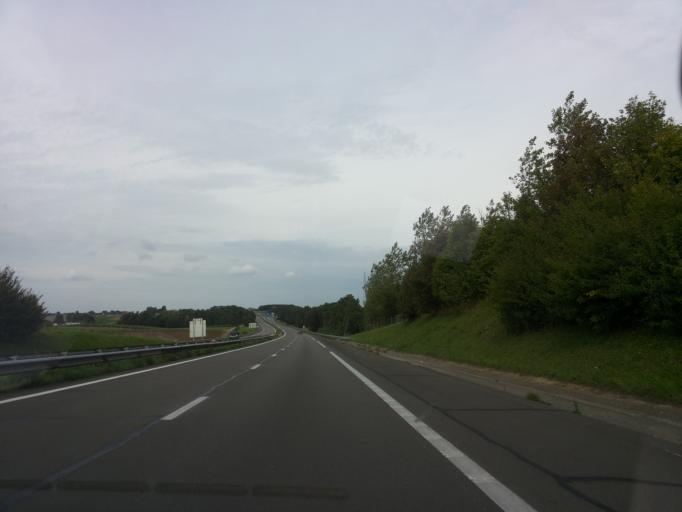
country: FR
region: Nord-Pas-de-Calais
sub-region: Departement du Pas-de-Calais
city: Therouanne
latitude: 50.6615
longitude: 2.2592
